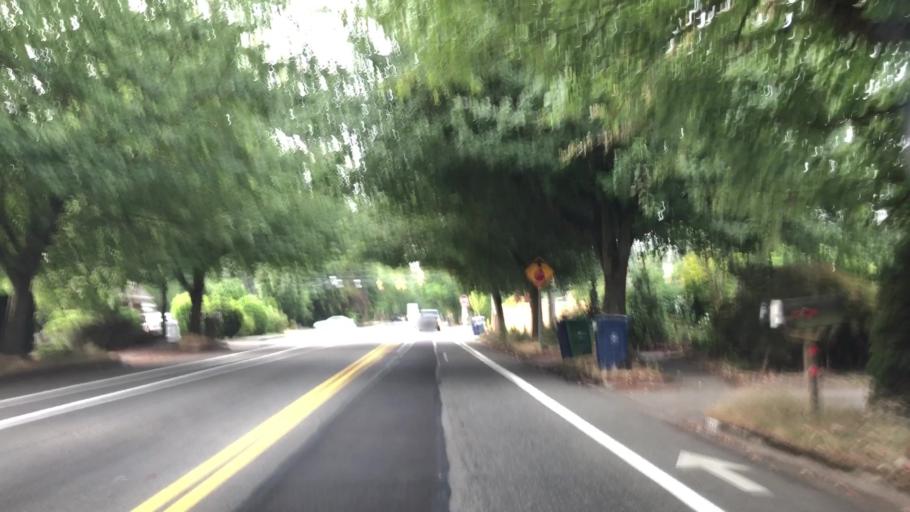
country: US
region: Washington
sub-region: King County
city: Redmond
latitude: 47.6763
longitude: -122.1639
